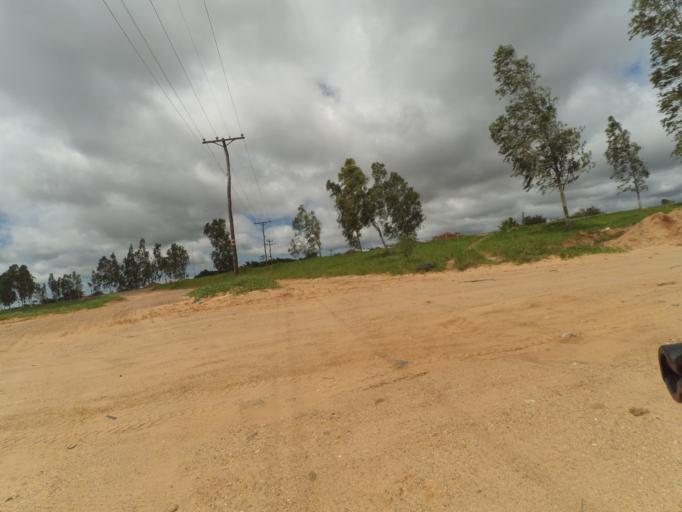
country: BO
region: Santa Cruz
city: Santa Rita
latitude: -17.9116
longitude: -63.2508
